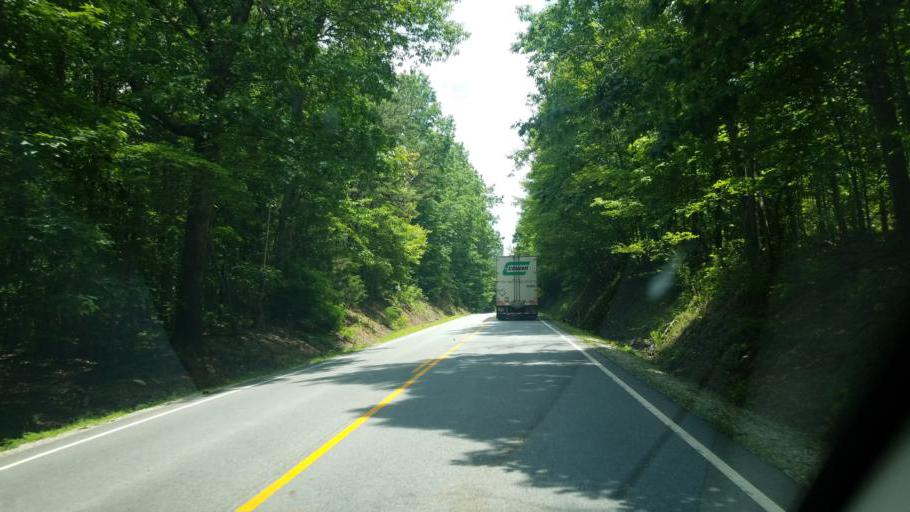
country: US
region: Virginia
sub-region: Amherst County
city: Amherst
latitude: 37.5711
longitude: -78.9059
